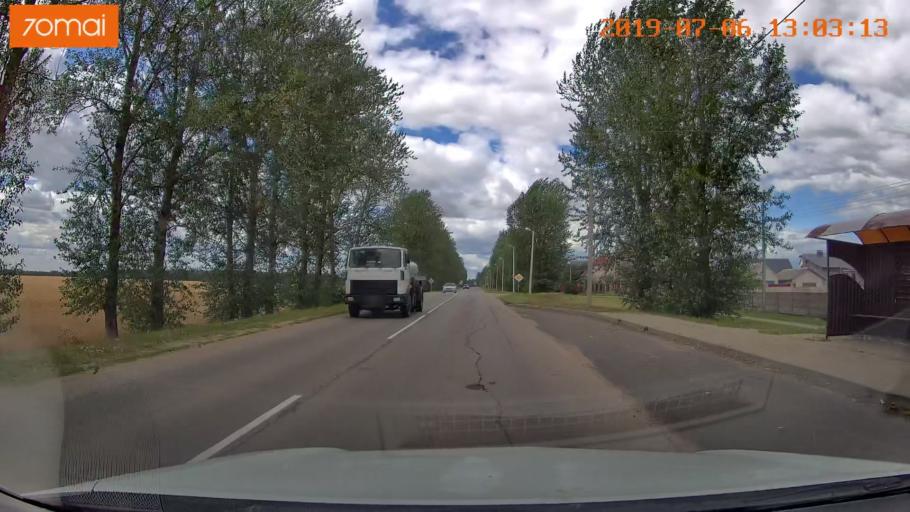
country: BY
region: Minsk
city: Dzyarzhynsk
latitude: 53.6884
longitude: 27.1052
